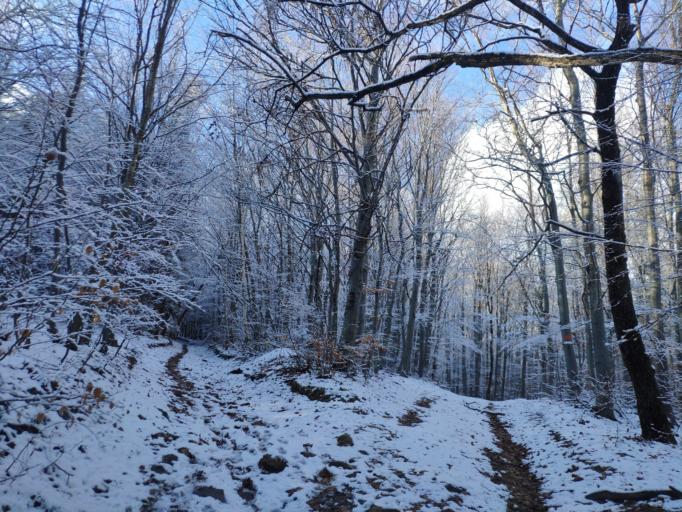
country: SK
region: Kosicky
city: Moldava nad Bodvou
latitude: 48.7395
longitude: 21.0991
